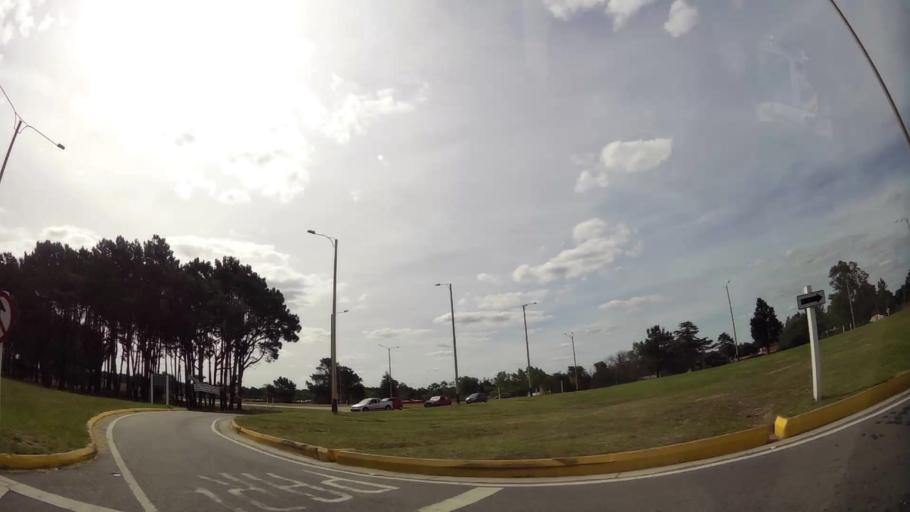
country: UY
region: Canelones
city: Empalme Olmos
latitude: -34.7890
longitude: -55.8945
